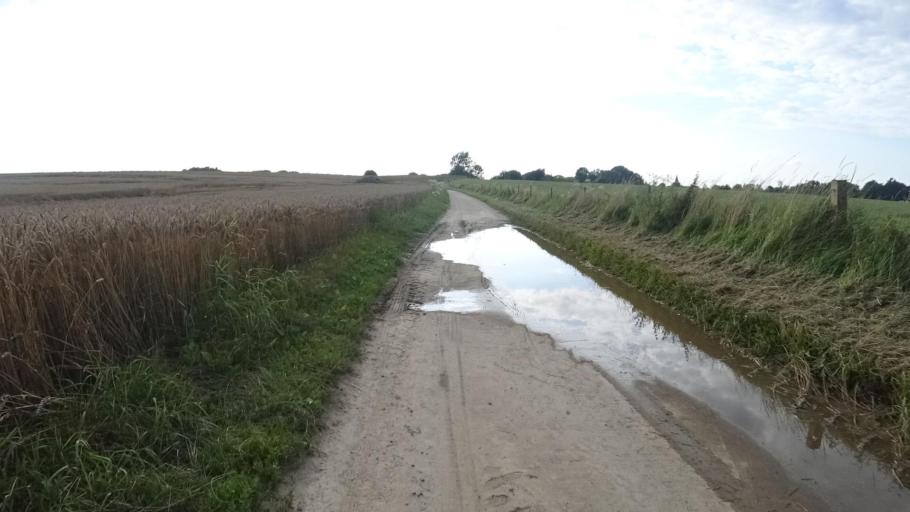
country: BE
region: Wallonia
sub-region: Province du Brabant Wallon
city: Walhain-Saint-Paul
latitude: 50.6378
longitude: 4.6858
